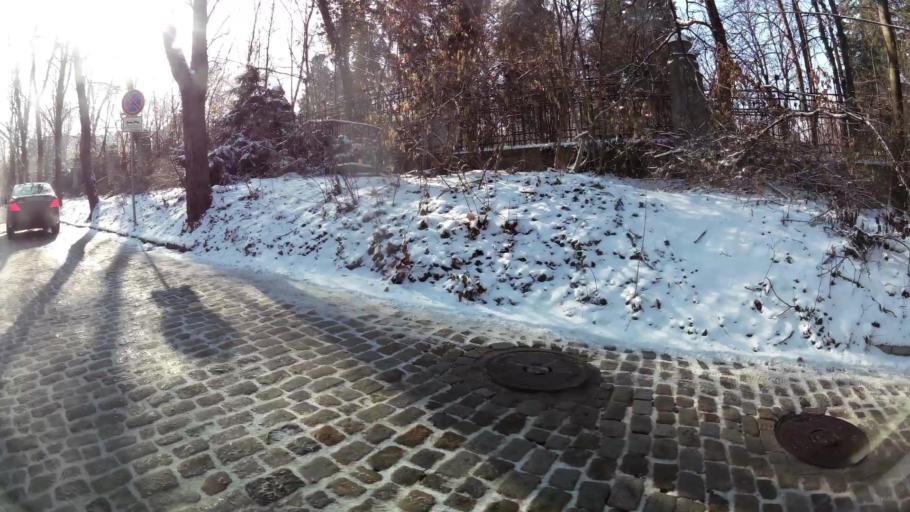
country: BG
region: Sofia-Capital
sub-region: Stolichna Obshtina
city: Sofia
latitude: 42.6753
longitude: 23.3275
